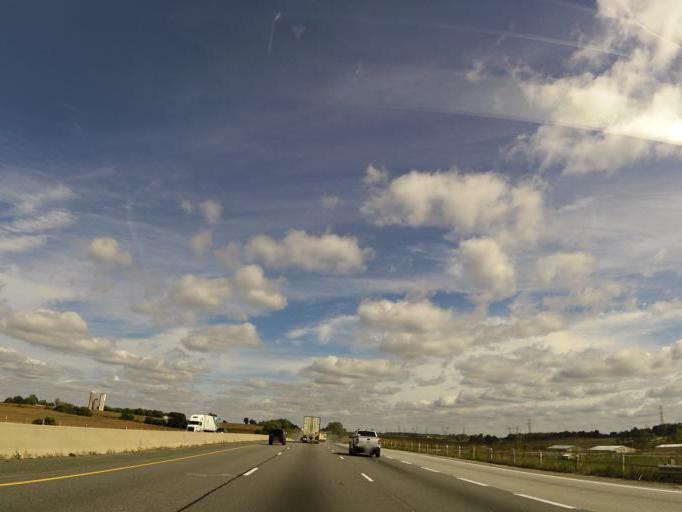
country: CA
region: Ontario
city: Ingersoll
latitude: 42.9758
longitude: -80.9501
